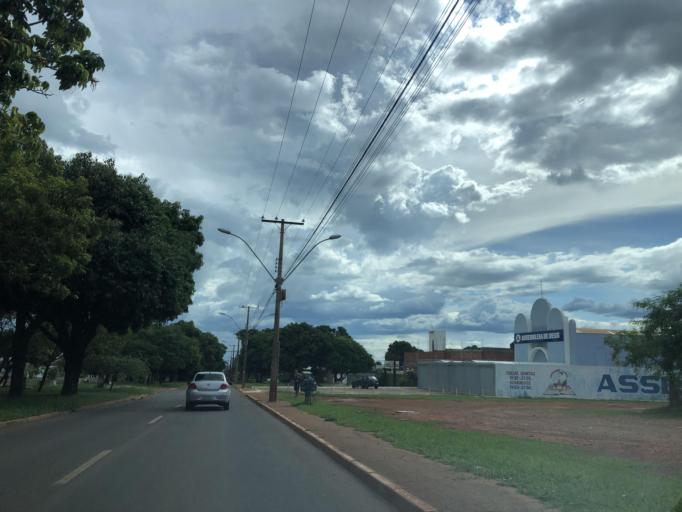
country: BR
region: Goias
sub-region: Luziania
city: Luziania
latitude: -16.0283
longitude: -48.0730
